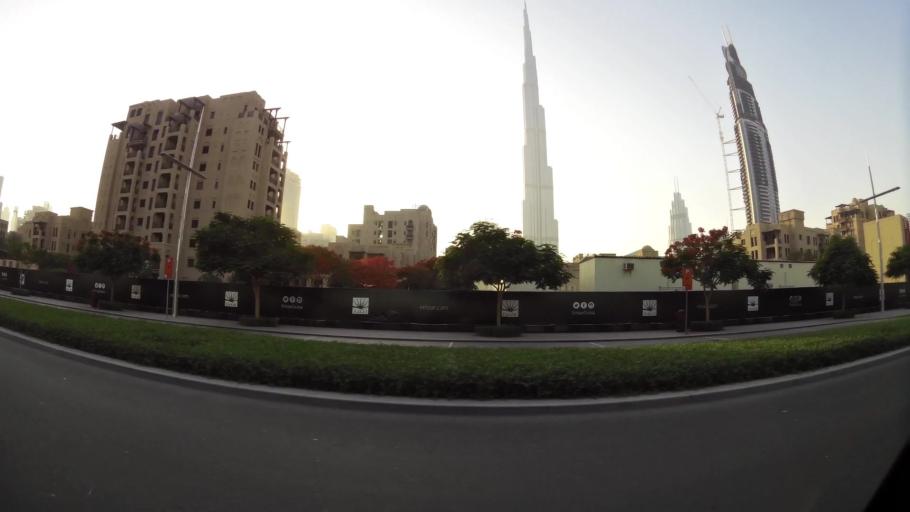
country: AE
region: Dubai
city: Dubai
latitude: 25.1907
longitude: 55.2786
